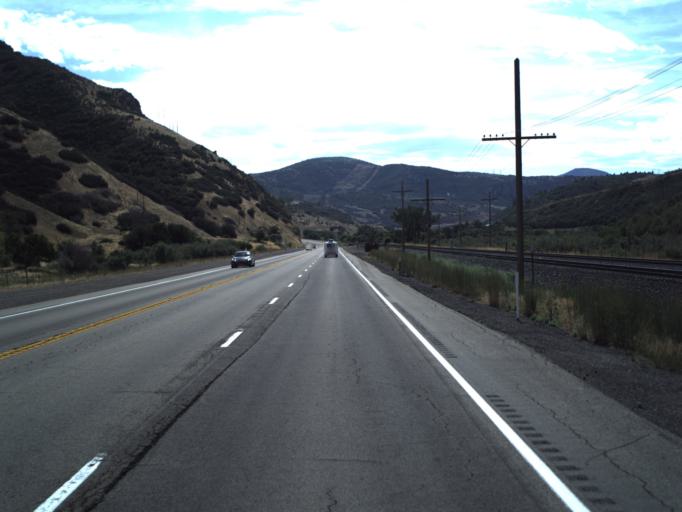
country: US
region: Utah
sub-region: Utah County
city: Mapleton
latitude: 40.0373
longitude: -111.5319
